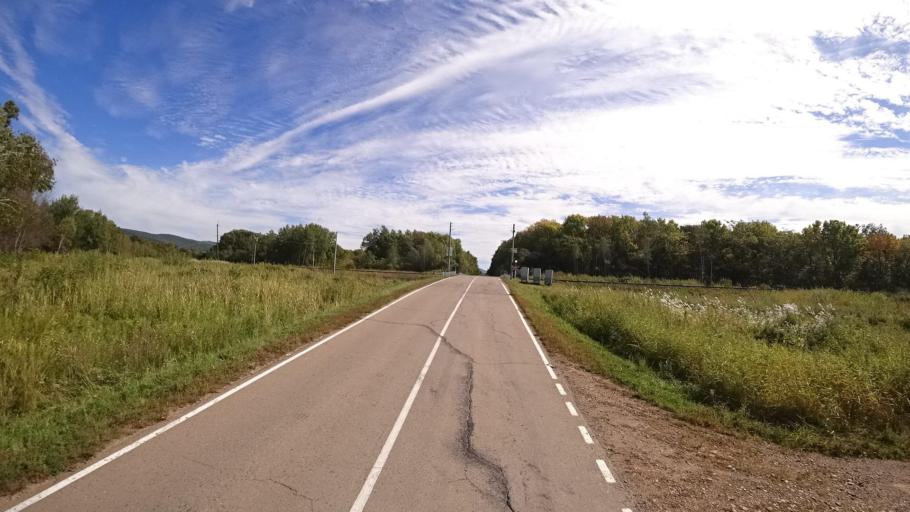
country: RU
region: Primorskiy
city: Yakovlevka
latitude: 44.4064
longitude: 133.5919
